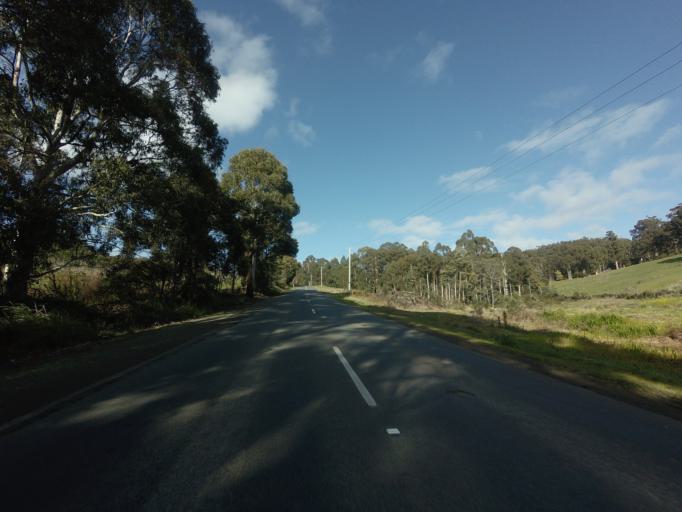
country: AU
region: Tasmania
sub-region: Huon Valley
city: Geeveston
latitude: -43.1928
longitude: 146.9585
